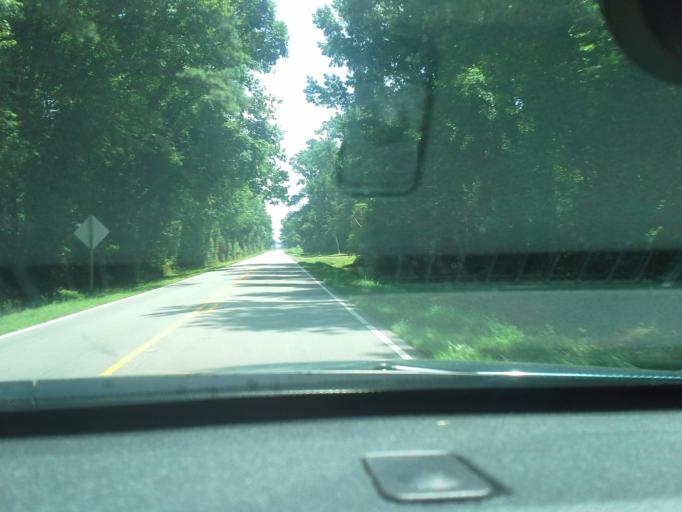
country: US
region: North Carolina
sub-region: Washington County
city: Plymouth
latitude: 35.9221
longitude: -76.6368
